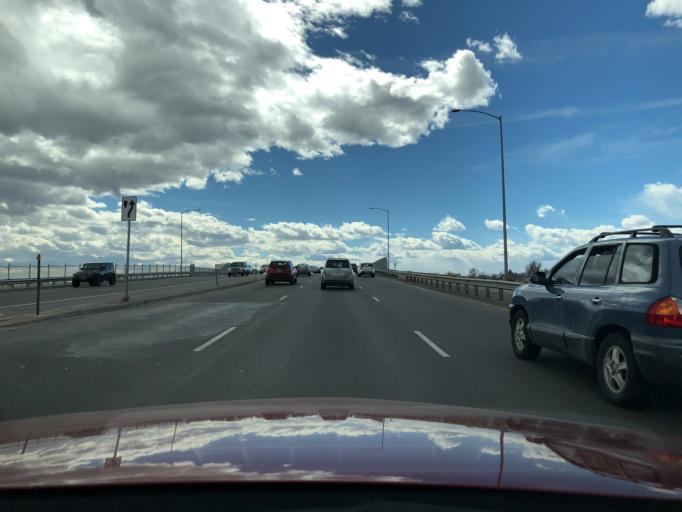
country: US
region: Colorado
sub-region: Adams County
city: Berkley
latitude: 39.8224
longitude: -105.0252
